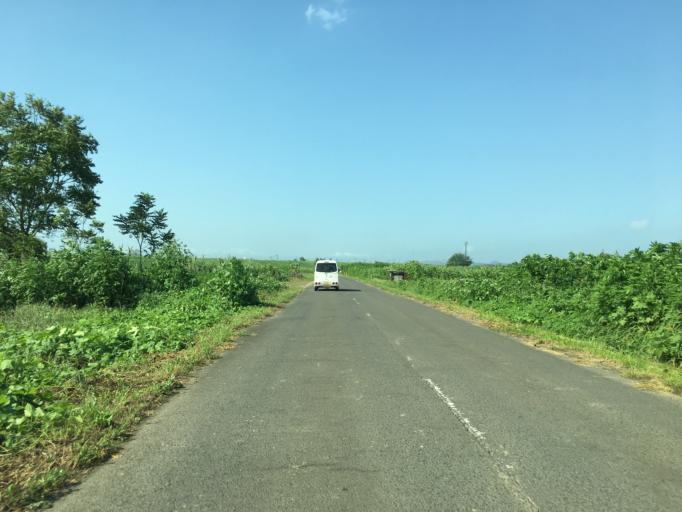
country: JP
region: Miyagi
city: Kakuda
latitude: 37.9657
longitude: 140.7884
